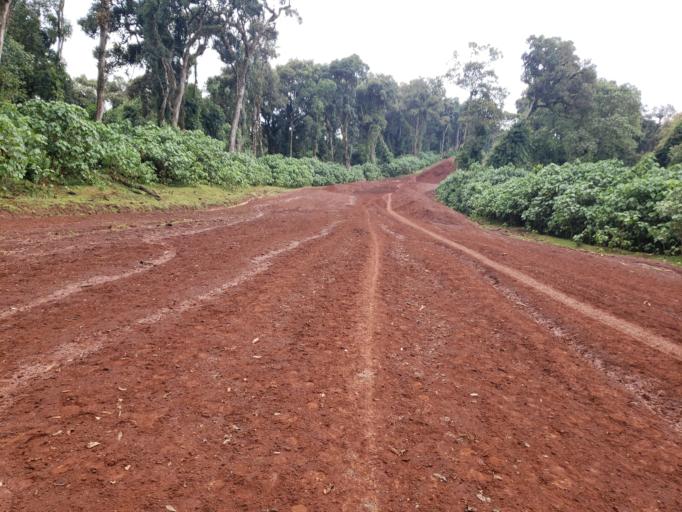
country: ET
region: Oromiya
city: Dodola
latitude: 6.5957
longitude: 39.4125
